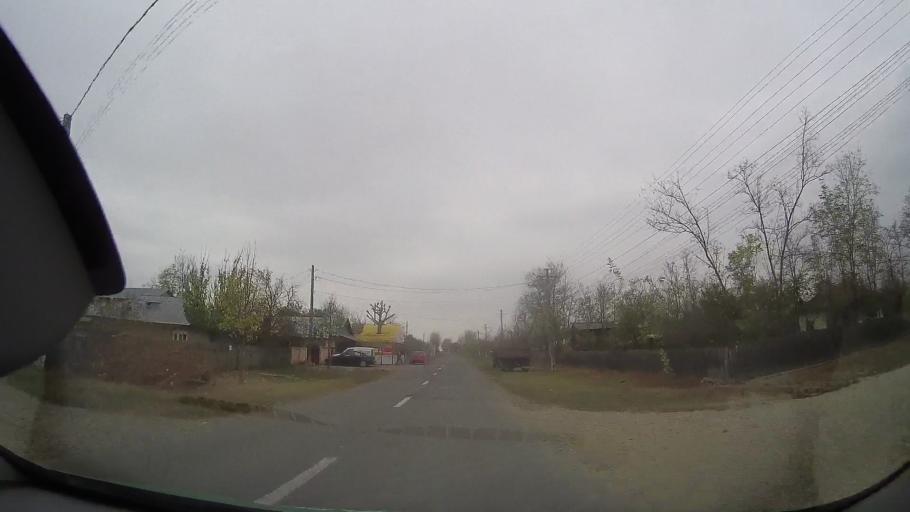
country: RO
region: Ialomita
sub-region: Comuna Grindu
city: Grindu
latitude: 44.7696
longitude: 26.8978
